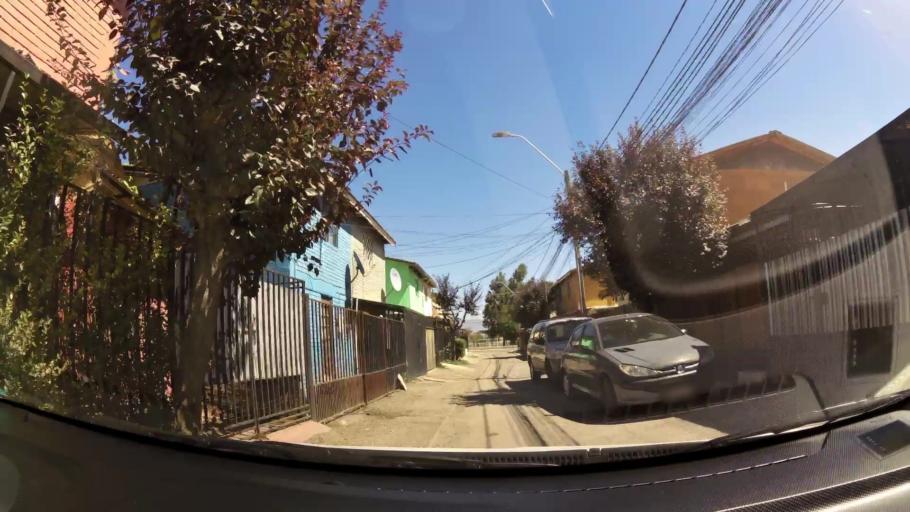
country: CL
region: O'Higgins
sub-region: Provincia de Cachapoal
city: Rancagua
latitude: -34.1630
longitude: -70.7120
